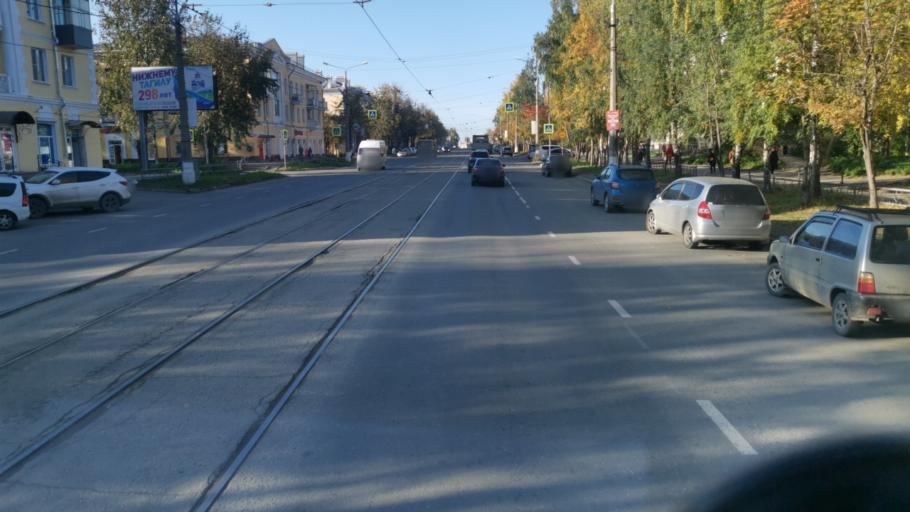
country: RU
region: Sverdlovsk
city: Nizhniy Tagil
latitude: 57.9195
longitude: 59.9434
